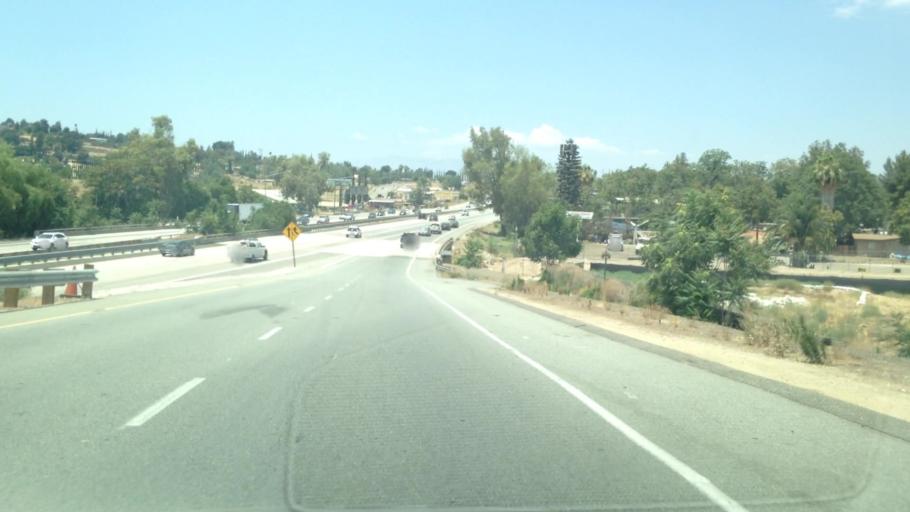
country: US
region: California
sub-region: Riverside County
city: Calimesa
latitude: 34.0173
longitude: -117.0962
